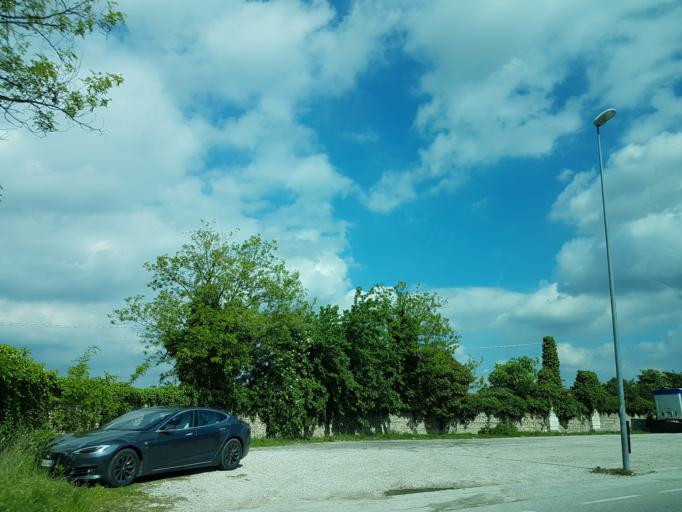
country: IT
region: Veneto
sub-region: Provincia di Vicenza
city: Bassano del Grappa
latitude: 45.7557
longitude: 11.7441
